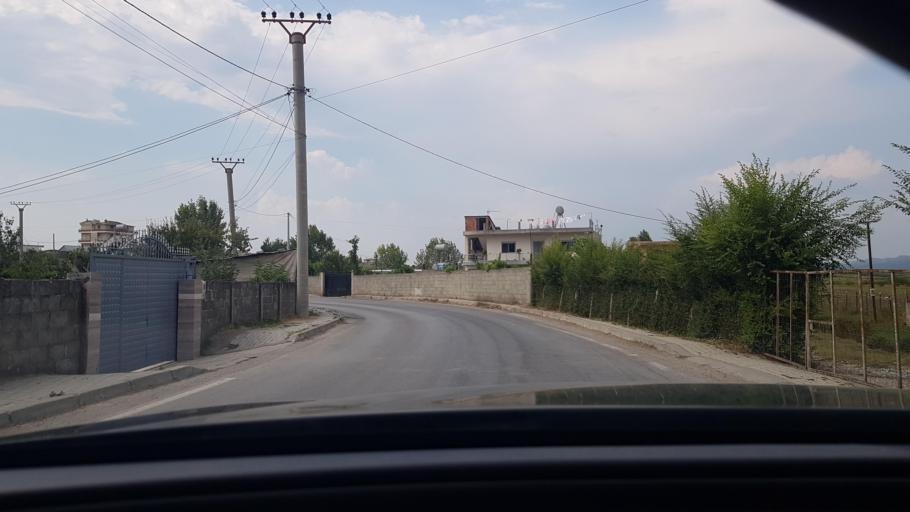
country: AL
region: Durres
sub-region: Rrethi i Durresit
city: Katundi i Ri
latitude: 41.4266
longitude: 19.5477
